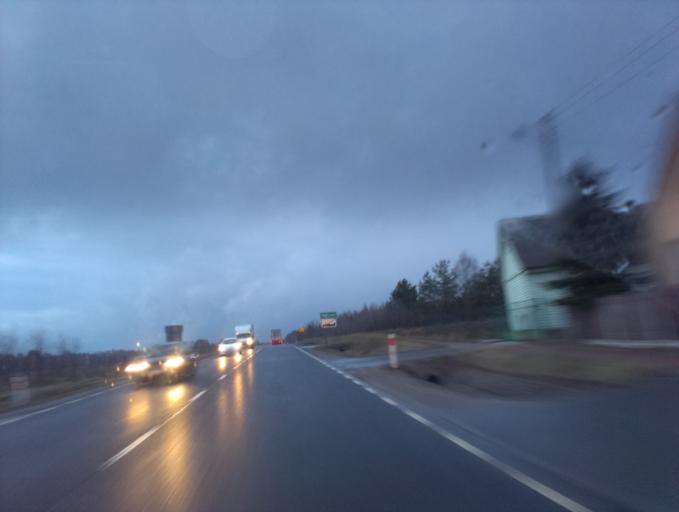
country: PL
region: Lodz Voivodeship
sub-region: Powiat opoczynski
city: Zarnow
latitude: 51.2162
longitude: 20.1919
